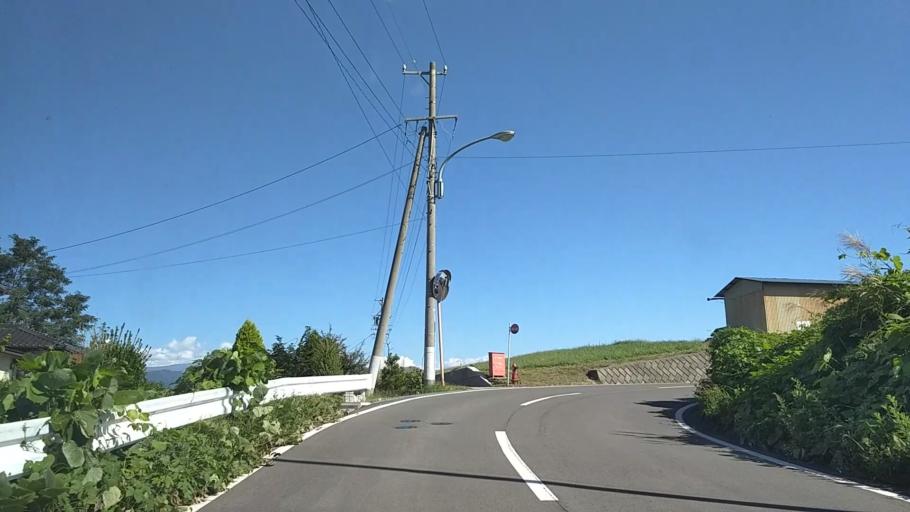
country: JP
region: Nagano
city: Nagano-shi
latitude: 36.5771
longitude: 138.1185
